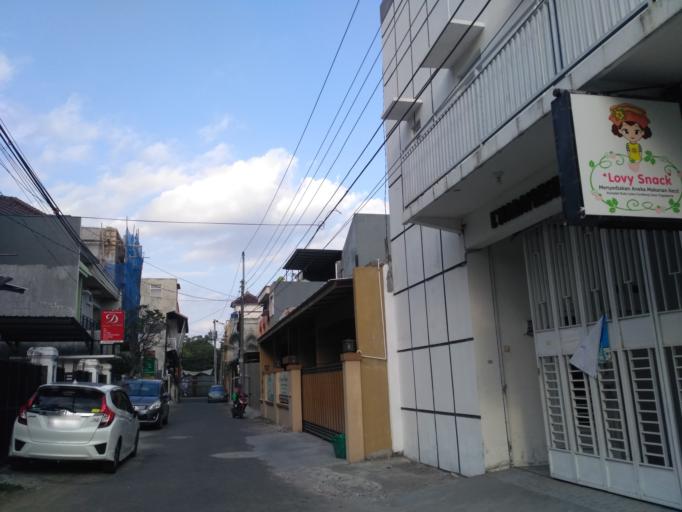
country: ID
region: Daerah Istimewa Yogyakarta
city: Depok
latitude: -7.7665
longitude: 110.4097
